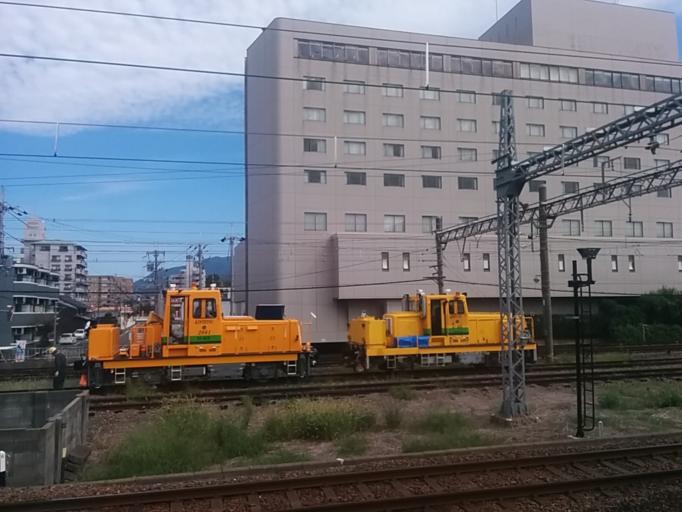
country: JP
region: Nara
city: Kashihara-shi
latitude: 34.4852
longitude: 135.7943
